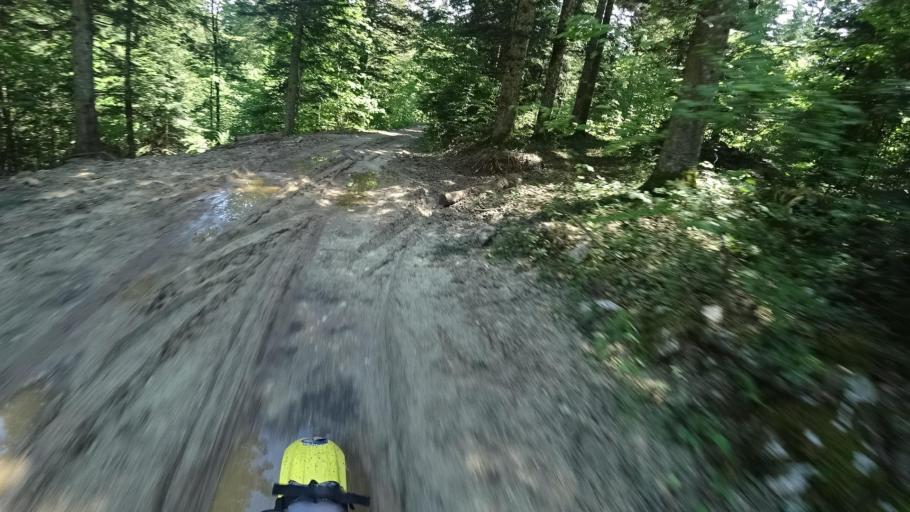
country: BA
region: Federation of Bosnia and Herzegovina
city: Stijena
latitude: 44.8122
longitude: 16.0276
